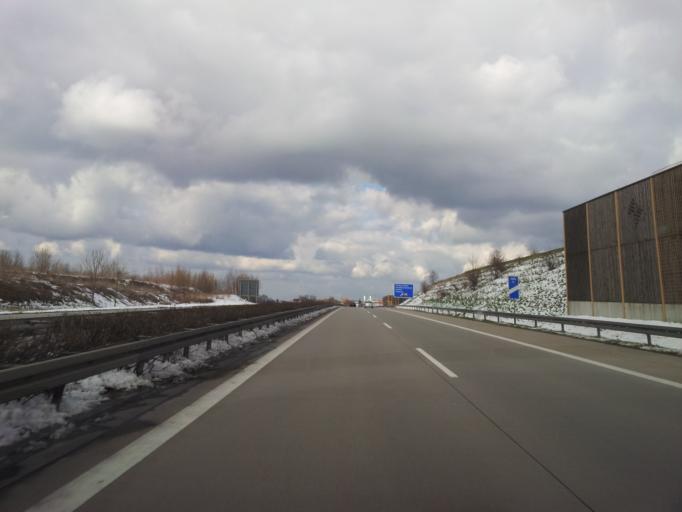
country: DE
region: Saxony
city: Stollberg
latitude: 50.7027
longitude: 12.7510
